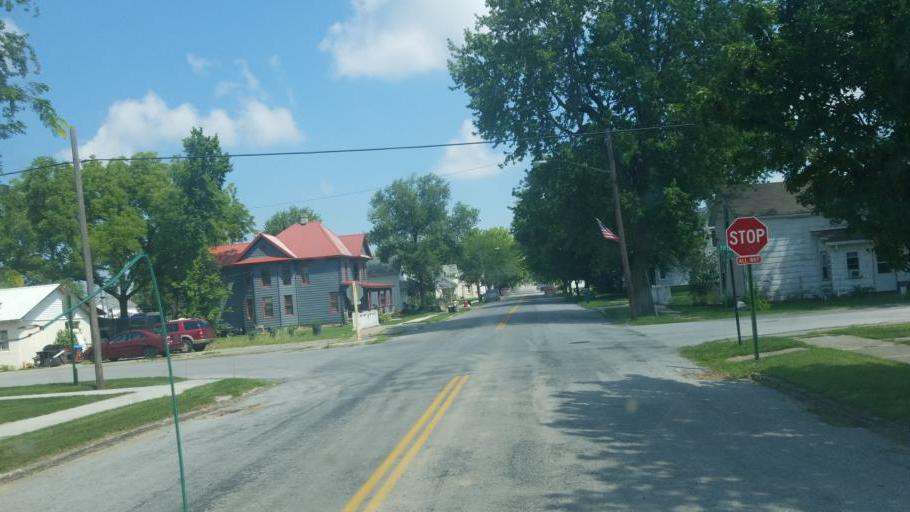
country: US
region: Ohio
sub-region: Hardin County
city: Ada
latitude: 40.7062
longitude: -83.9210
